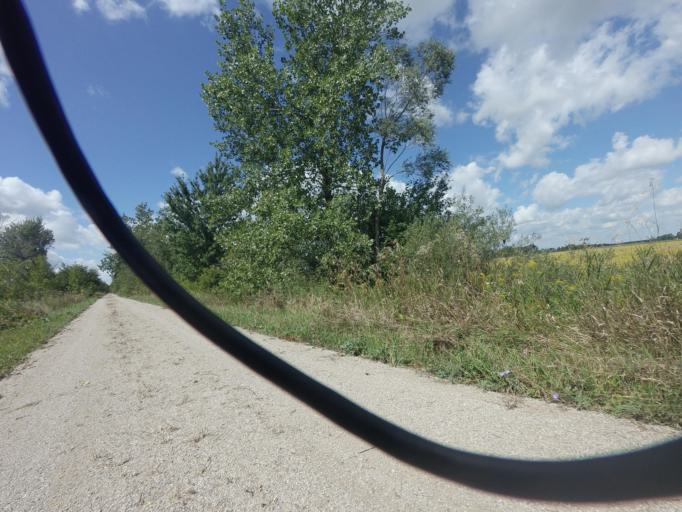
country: CA
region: Ontario
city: North Perth
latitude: 43.5654
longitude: -80.9653
